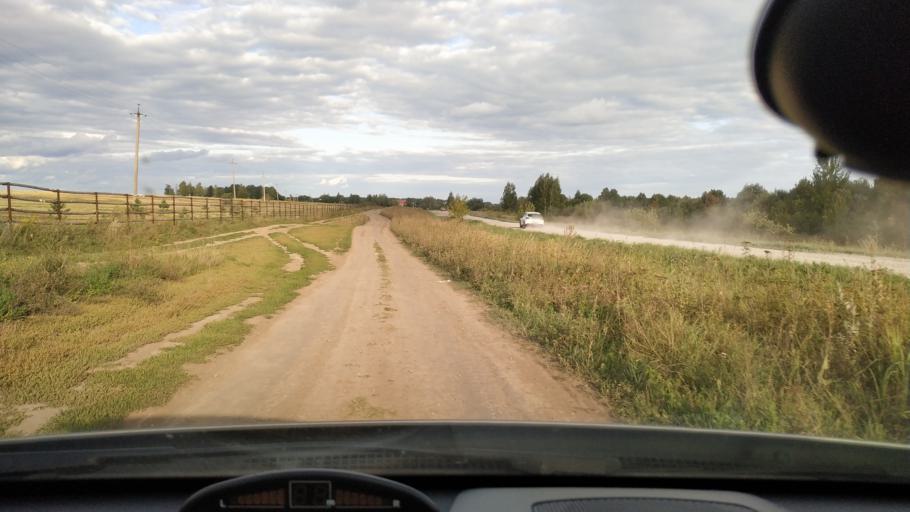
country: RU
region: Rjazan
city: Polyany
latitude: 54.5649
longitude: 39.8668
